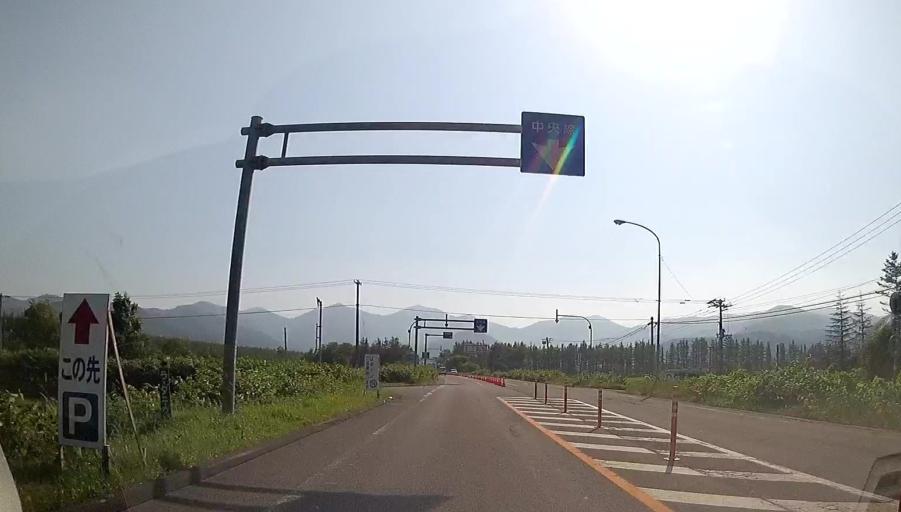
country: JP
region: Hokkaido
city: Otofuke
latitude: 42.9934
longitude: 142.8491
